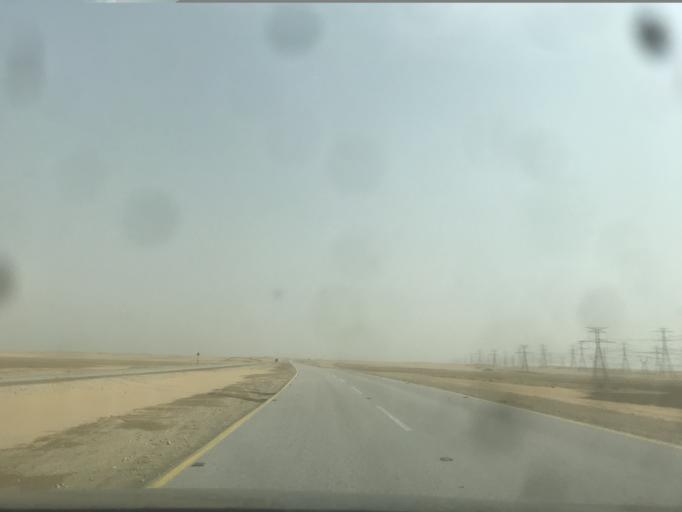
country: SA
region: Eastern Province
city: Abqaiq
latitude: 25.9134
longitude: 49.8016
